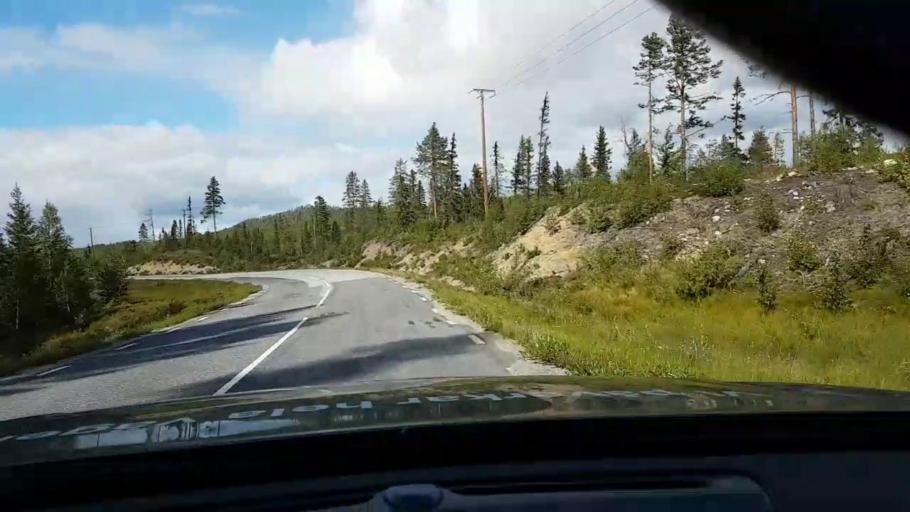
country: SE
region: Vaesterbotten
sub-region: Asele Kommun
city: Asele
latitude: 63.8250
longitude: 17.4763
